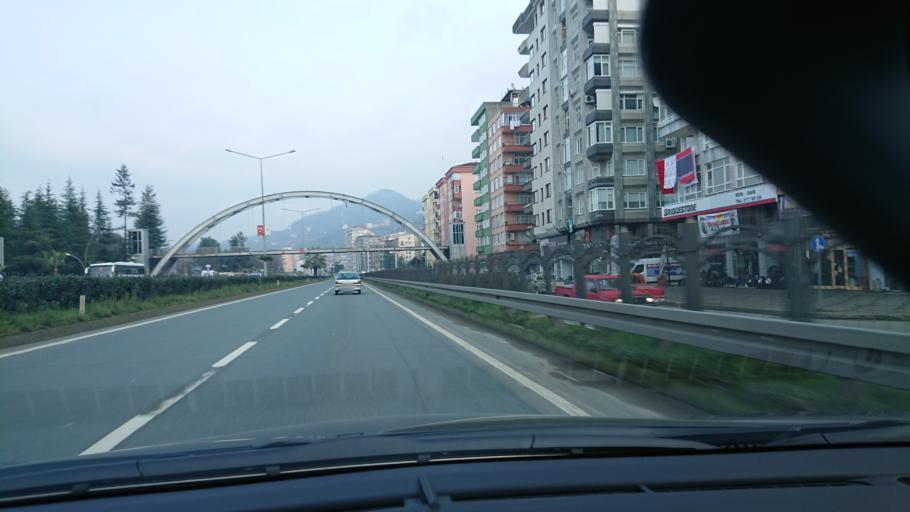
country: TR
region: Rize
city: Rize
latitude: 41.0257
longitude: 40.5291
